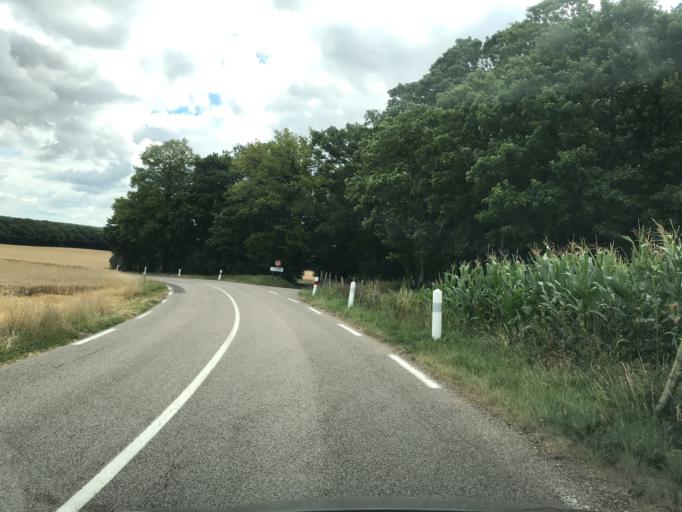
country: FR
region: Haute-Normandie
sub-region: Departement de l'Eure
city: Menilles
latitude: 49.0371
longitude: 1.2968
